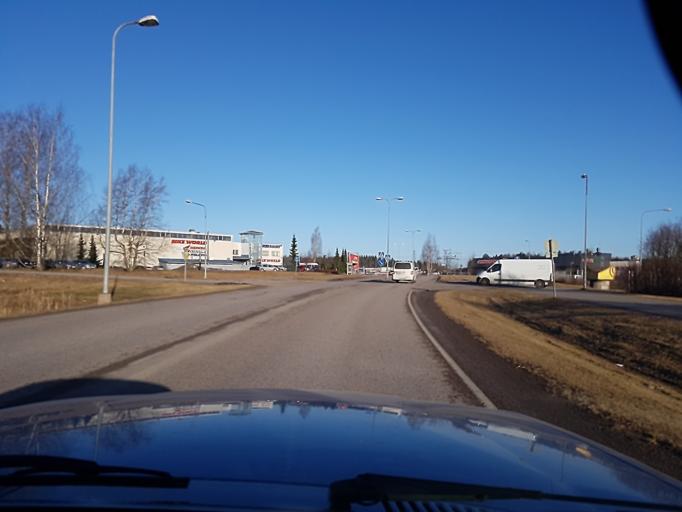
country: FI
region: Uusimaa
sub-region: Helsinki
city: Teekkarikylae
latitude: 60.2955
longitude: 24.8929
